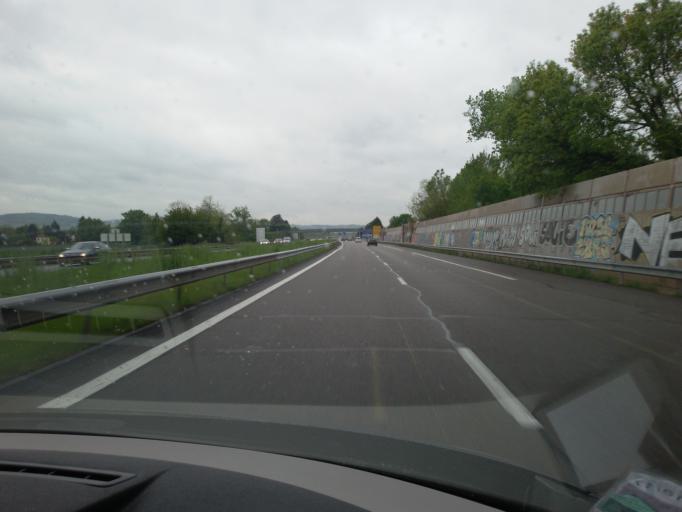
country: FR
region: Rhone-Alpes
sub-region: Departement du Rhone
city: Les Cheres
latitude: 45.8835
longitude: 4.7382
